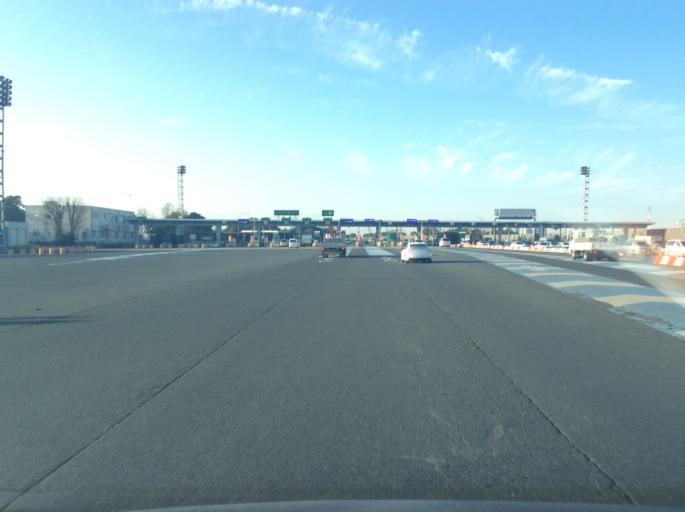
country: JP
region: Chiba
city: Nagareyama
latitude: 35.8668
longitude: 139.8841
